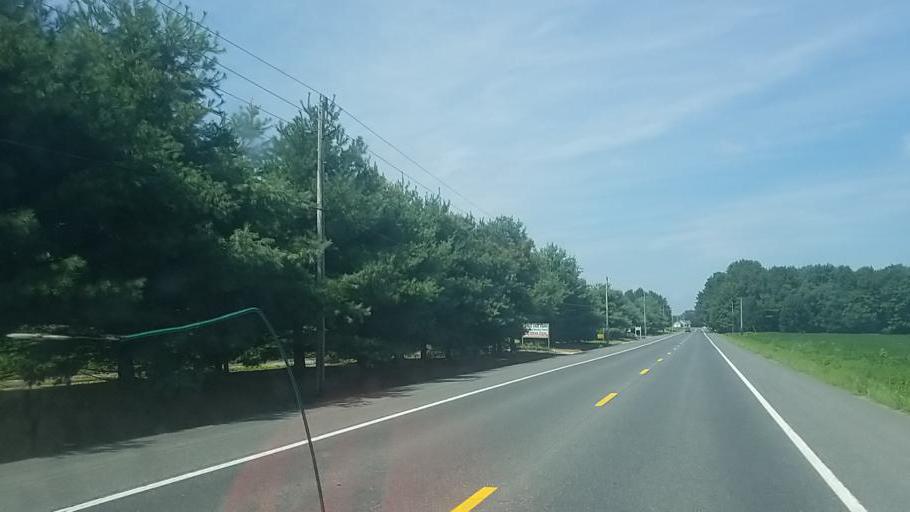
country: US
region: Delaware
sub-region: Sussex County
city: Bridgeville
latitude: 38.8242
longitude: -75.6342
